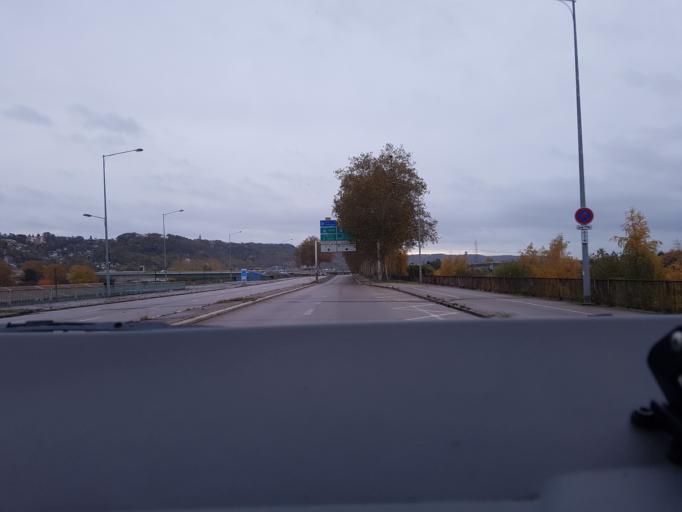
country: FR
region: Haute-Normandie
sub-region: Departement de la Seine-Maritime
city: Rouen
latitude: 49.4330
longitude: 1.0959
